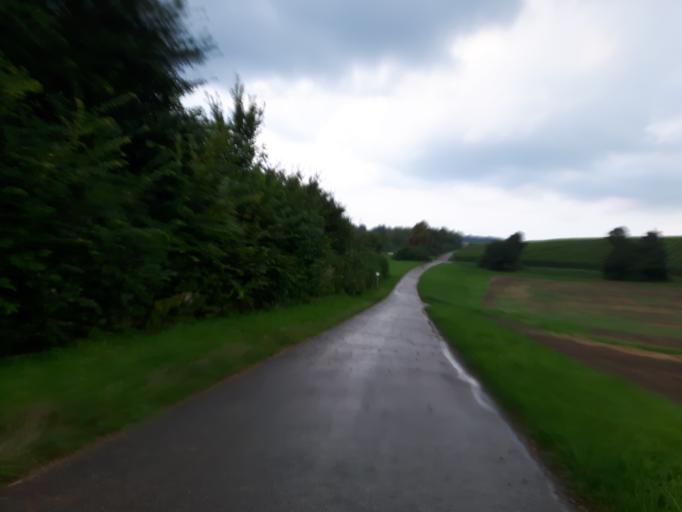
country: DE
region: Baden-Wuerttemberg
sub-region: Regierungsbezirk Stuttgart
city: Weinsberg
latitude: 49.1714
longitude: 9.2964
